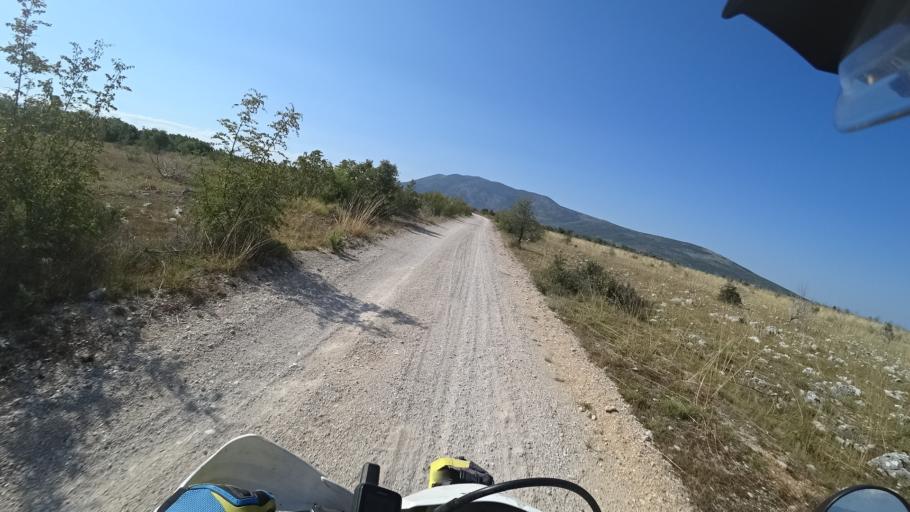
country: HR
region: Sibensko-Kniniska
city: Knin
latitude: 43.9878
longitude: 16.1914
